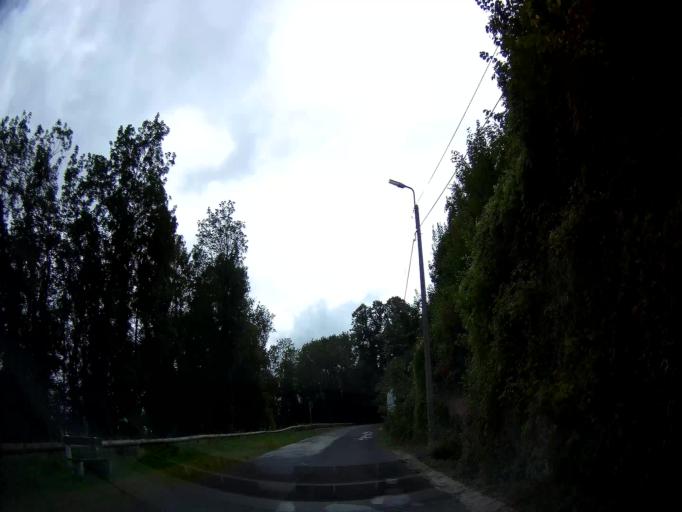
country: BE
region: Wallonia
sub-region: Province de Liege
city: Limbourg
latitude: 50.6151
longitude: 5.9412
